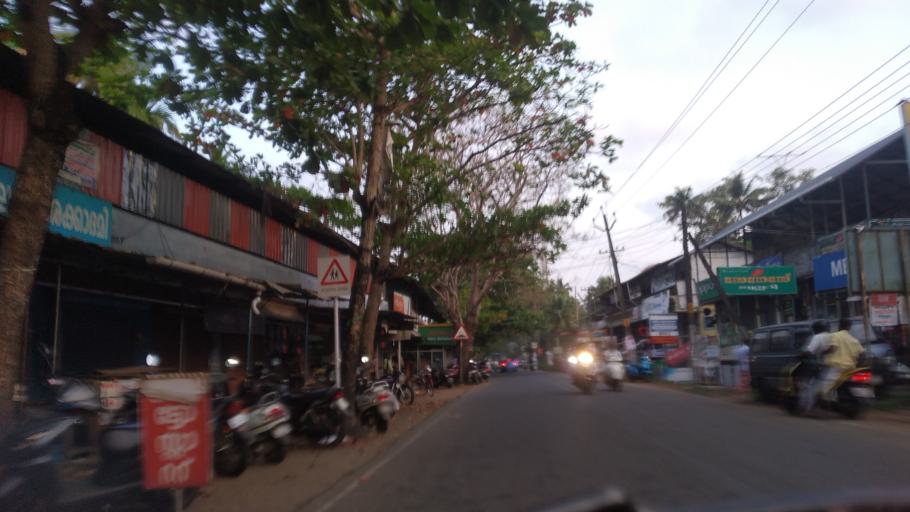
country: IN
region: Kerala
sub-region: Thrissur District
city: Kodungallur
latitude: 10.2231
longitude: 76.1574
